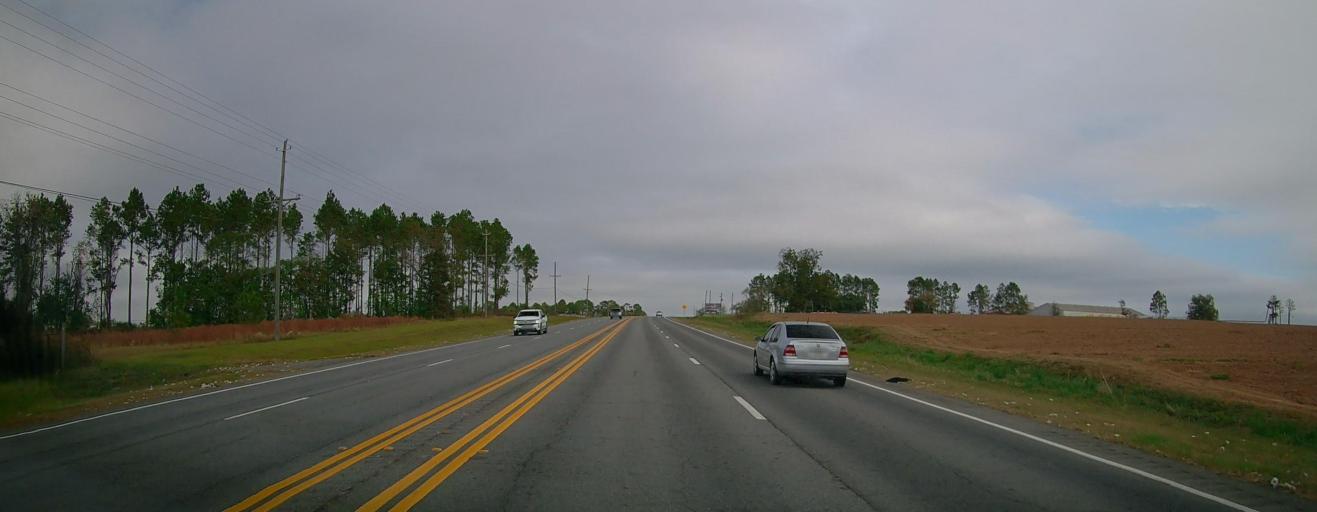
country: US
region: Georgia
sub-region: Tift County
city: Omega
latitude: 31.3715
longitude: -83.5694
